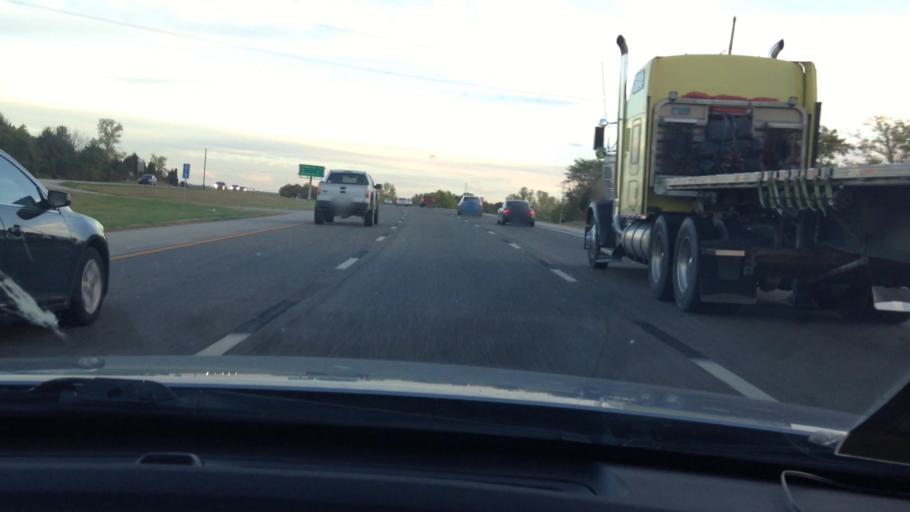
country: US
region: Kansas
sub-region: Wyandotte County
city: Edwardsville
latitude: 39.0965
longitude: -94.8099
